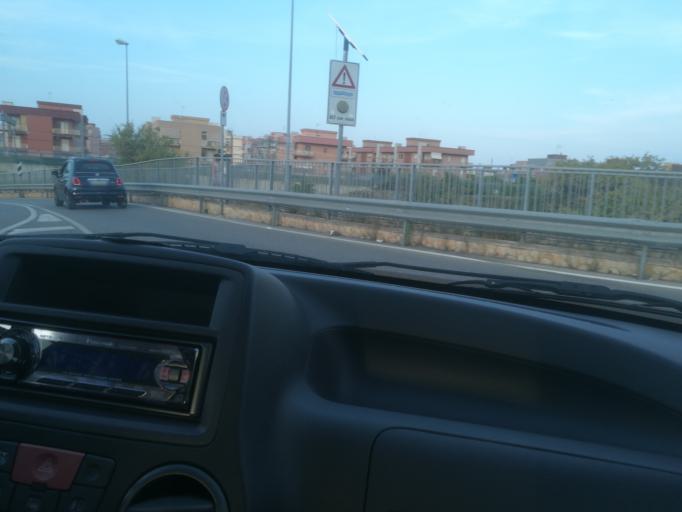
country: IT
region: Apulia
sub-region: Provincia di Bari
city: Monopoli
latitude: 40.9448
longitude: 17.3018
